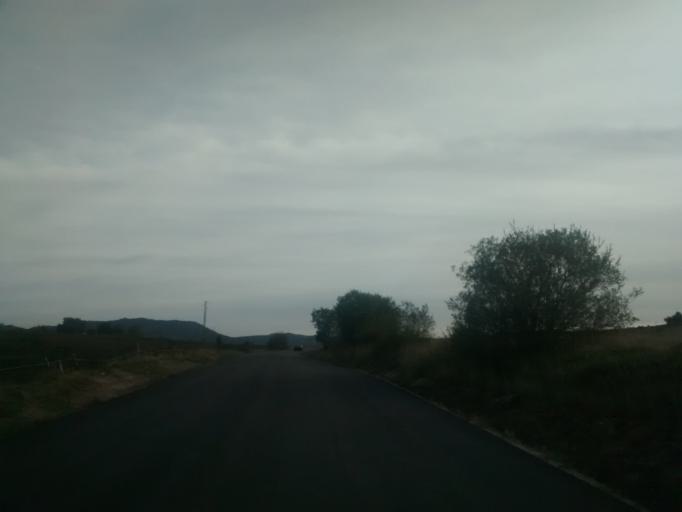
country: ES
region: Castille and Leon
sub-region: Provincia de Burgos
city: Arija
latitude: 42.9861
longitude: -3.9419
